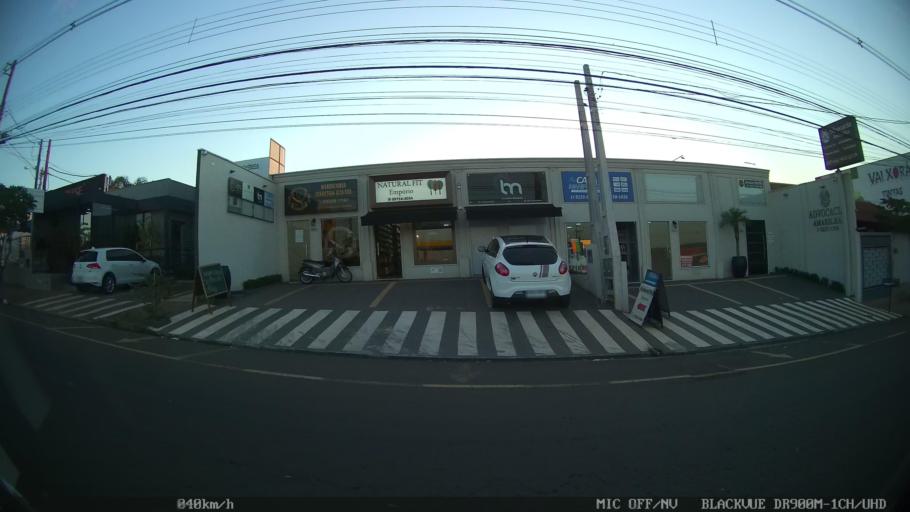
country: BR
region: Sao Paulo
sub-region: Sao Jose Do Rio Preto
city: Sao Jose do Rio Preto
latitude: -20.7883
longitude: -49.3441
